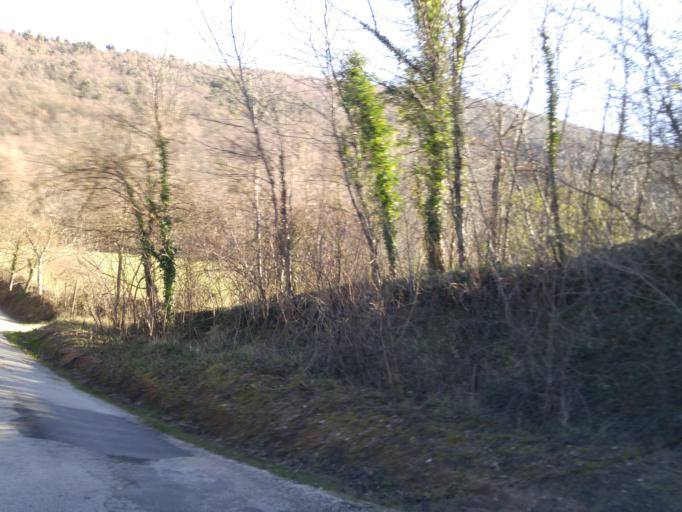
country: IT
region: The Marches
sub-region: Provincia di Pesaro e Urbino
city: Canavaccio
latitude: 43.6576
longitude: 12.7511
